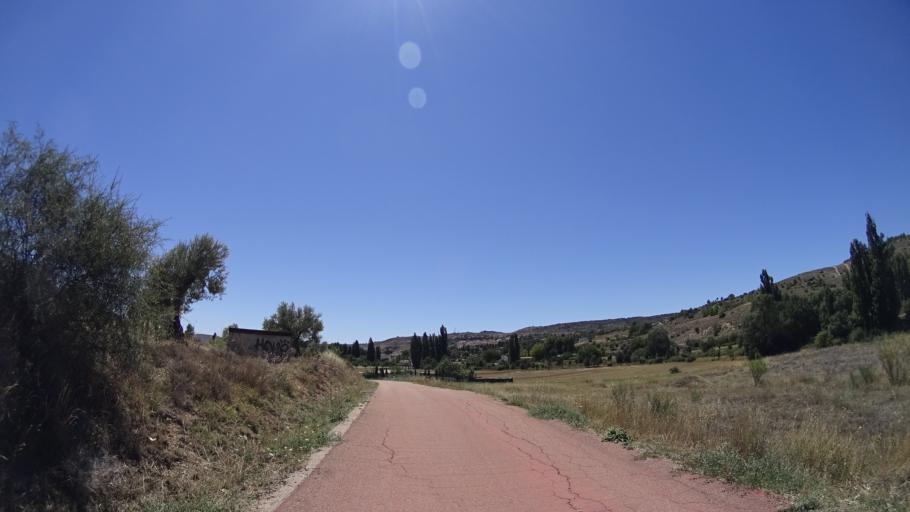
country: ES
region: Madrid
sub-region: Provincia de Madrid
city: Carabana
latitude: 40.2644
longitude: -3.2243
